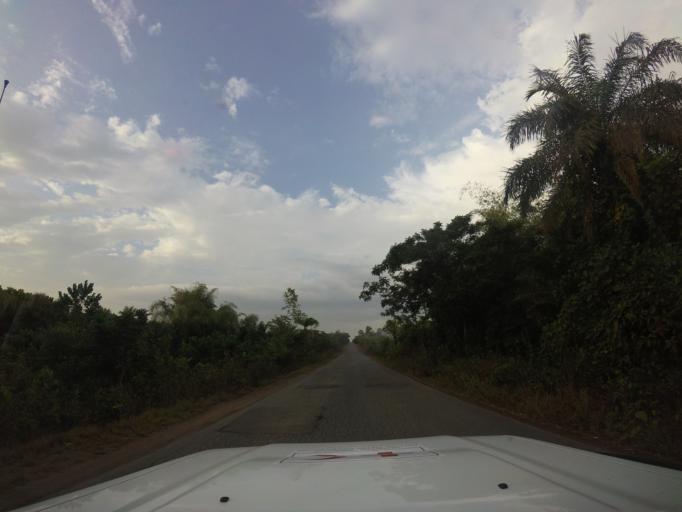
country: LR
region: Bomi
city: Tubmanburg
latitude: 6.7062
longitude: -10.8719
